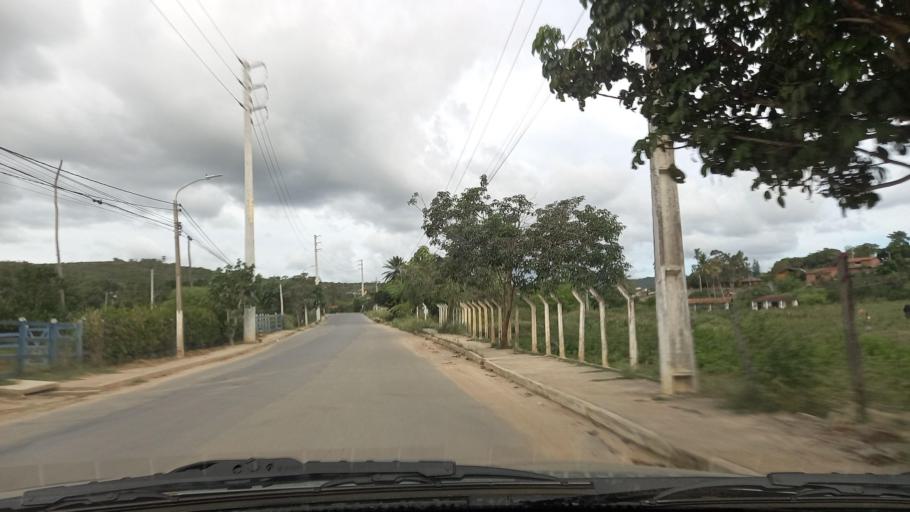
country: BR
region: Pernambuco
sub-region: Gravata
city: Gravata
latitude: -8.2058
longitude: -35.5587
